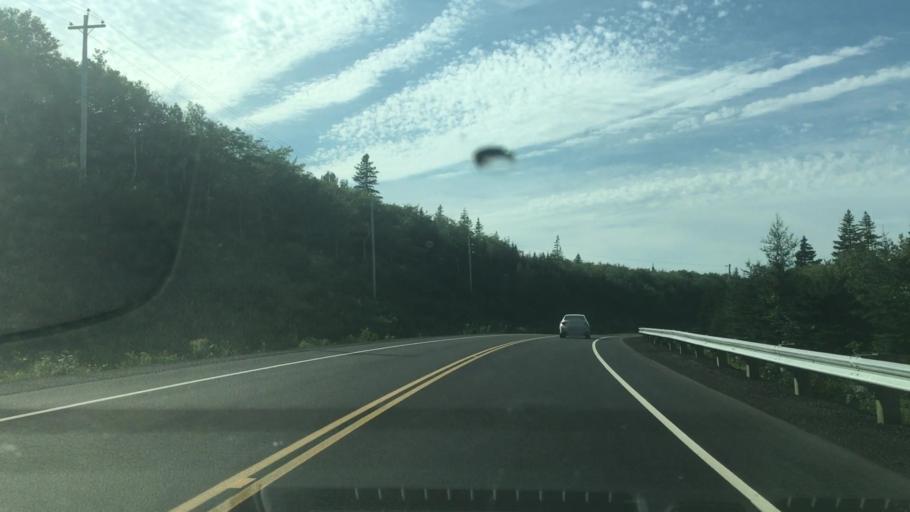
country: CA
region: Nova Scotia
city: Sydney Mines
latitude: 46.8372
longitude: -60.3830
